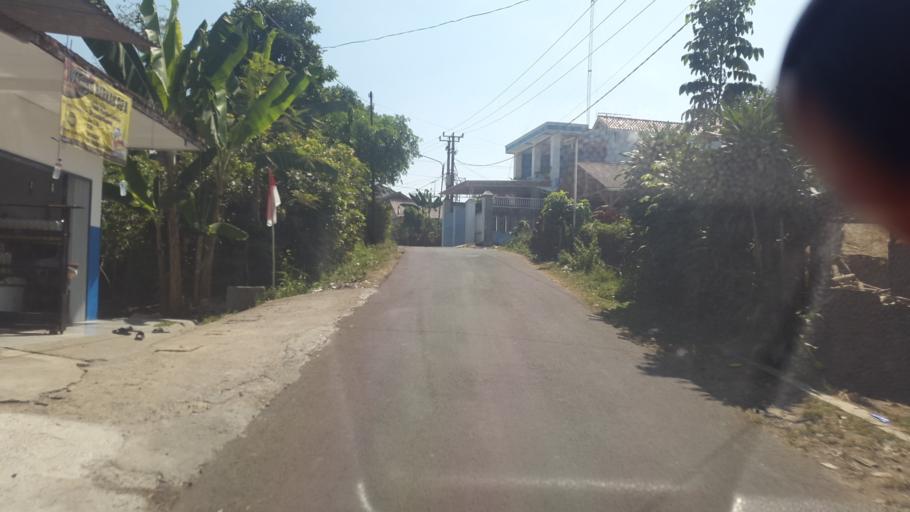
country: ID
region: West Java
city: Cicurug
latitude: -6.8409
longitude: 106.7048
